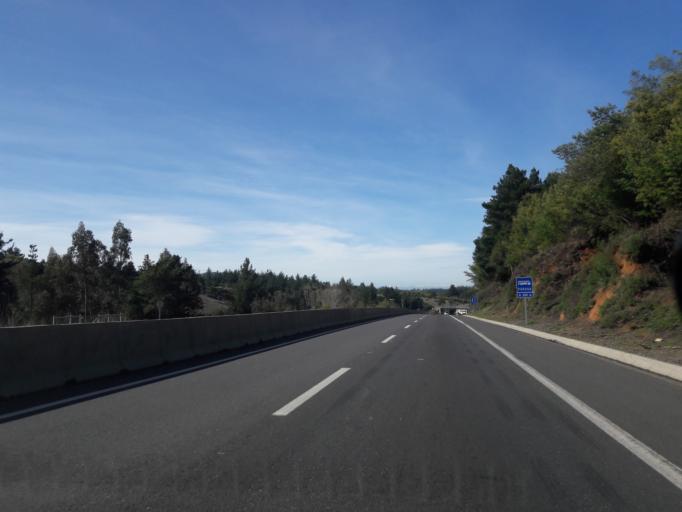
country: CL
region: Biobio
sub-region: Provincia de Biobio
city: Yumbel
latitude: -36.9648
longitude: -72.7007
